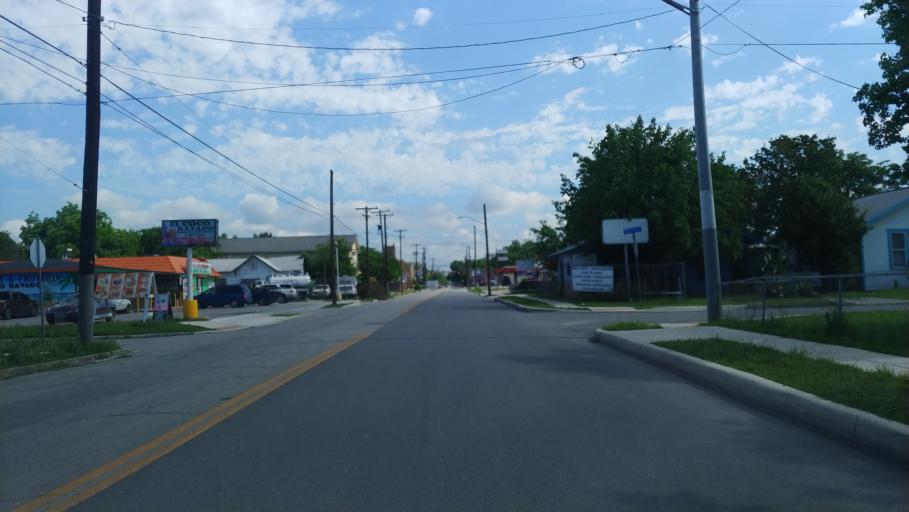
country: US
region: Texas
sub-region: Bexar County
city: San Antonio
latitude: 29.4514
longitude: -98.5241
